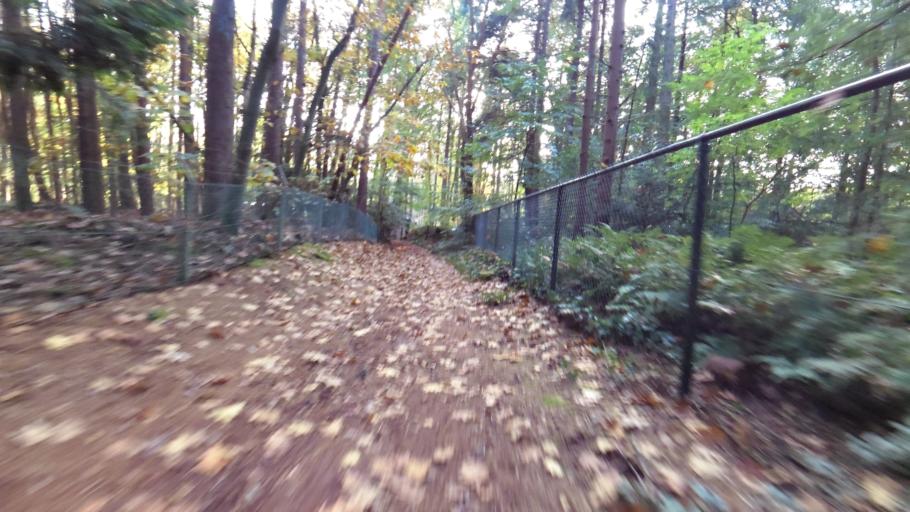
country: NL
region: Gelderland
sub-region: Gemeente Ede
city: Lunteren
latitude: 52.0910
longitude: 5.6372
